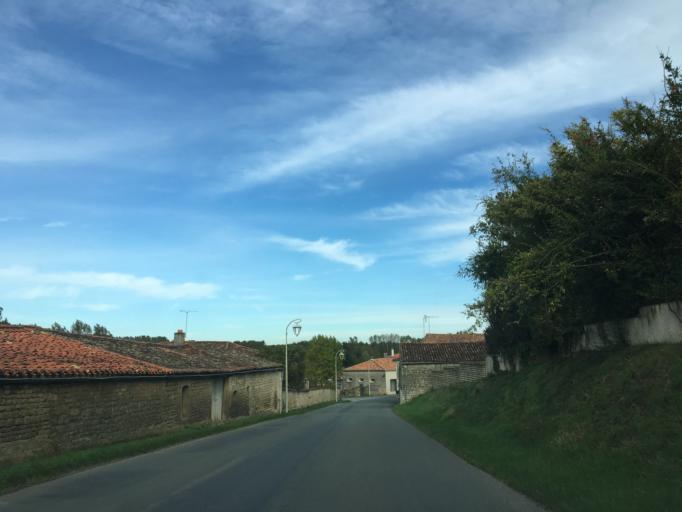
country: FR
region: Poitou-Charentes
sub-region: Departement de la Charente-Maritime
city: Aulnay
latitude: 46.0646
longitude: -0.4139
